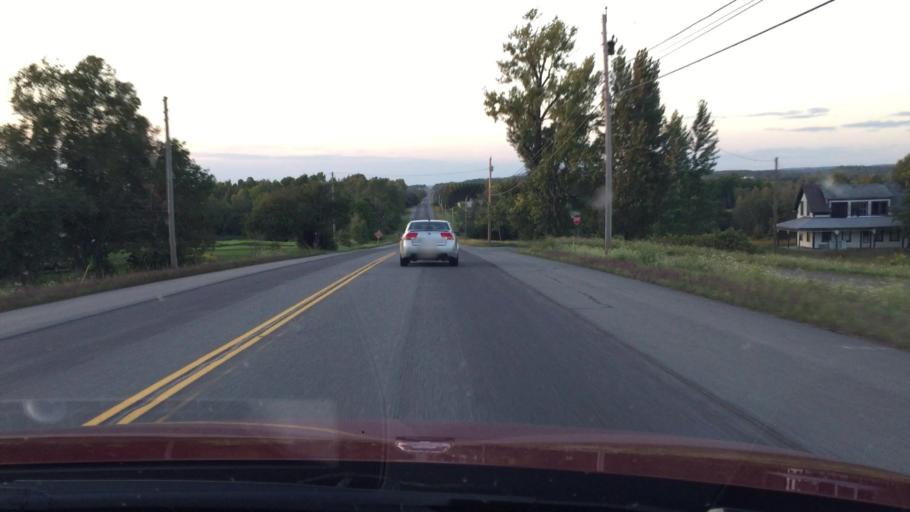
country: US
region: Maine
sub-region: Aroostook County
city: Houlton
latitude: 46.3538
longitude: -67.8421
